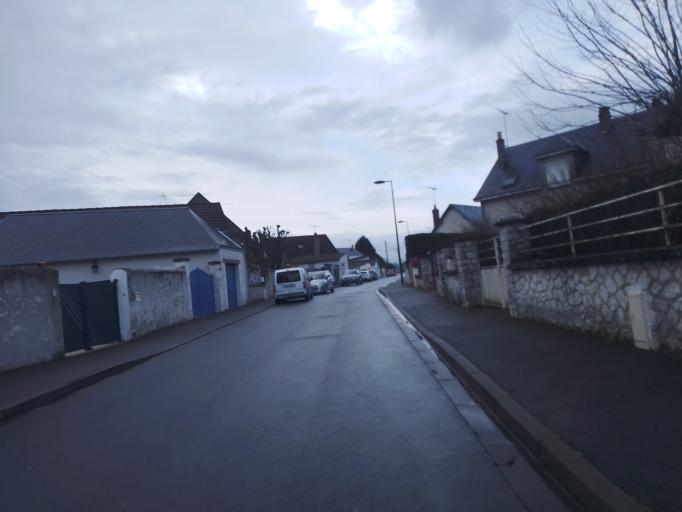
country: FR
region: Centre
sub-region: Departement du Loir-et-Cher
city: Blois
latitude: 47.5983
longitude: 1.3458
